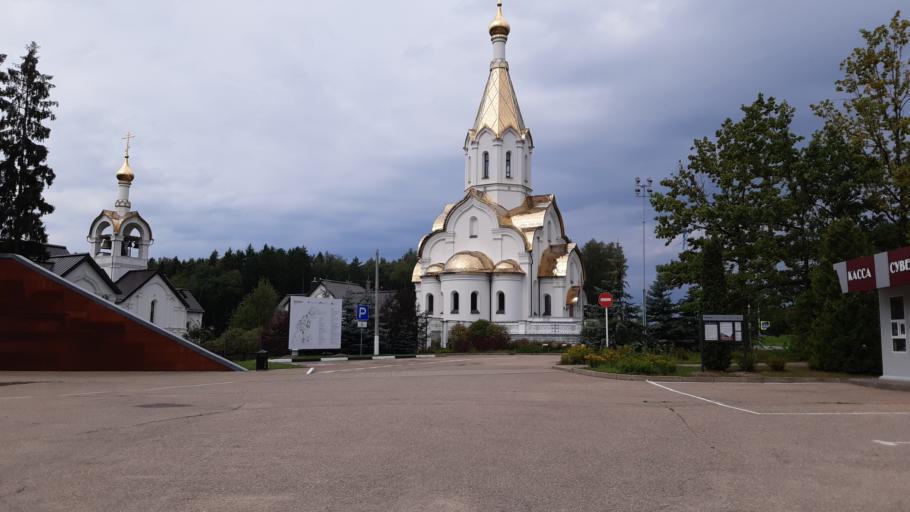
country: RU
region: Smolensk
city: Katyn'
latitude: 54.7758
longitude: 31.7887
